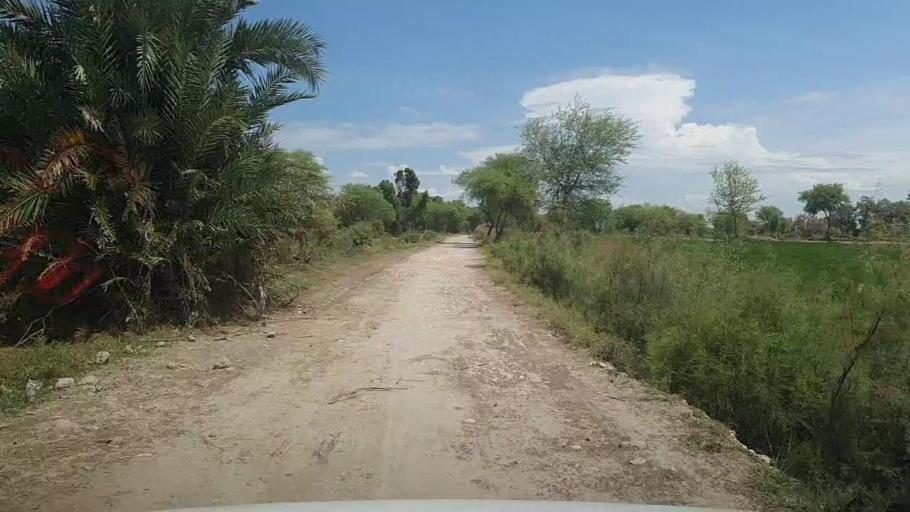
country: PK
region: Sindh
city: Kandhkot
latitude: 28.3410
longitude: 69.2412
